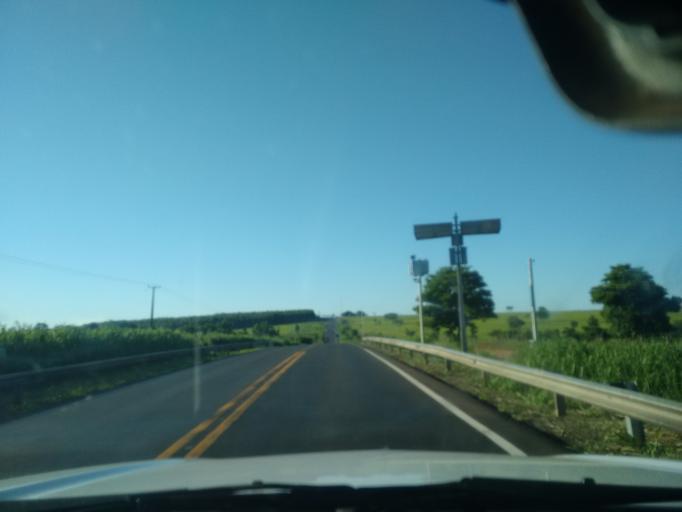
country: BR
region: Mato Grosso do Sul
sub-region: Eldorado
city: Eldorado
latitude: -23.8772
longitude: -54.3218
